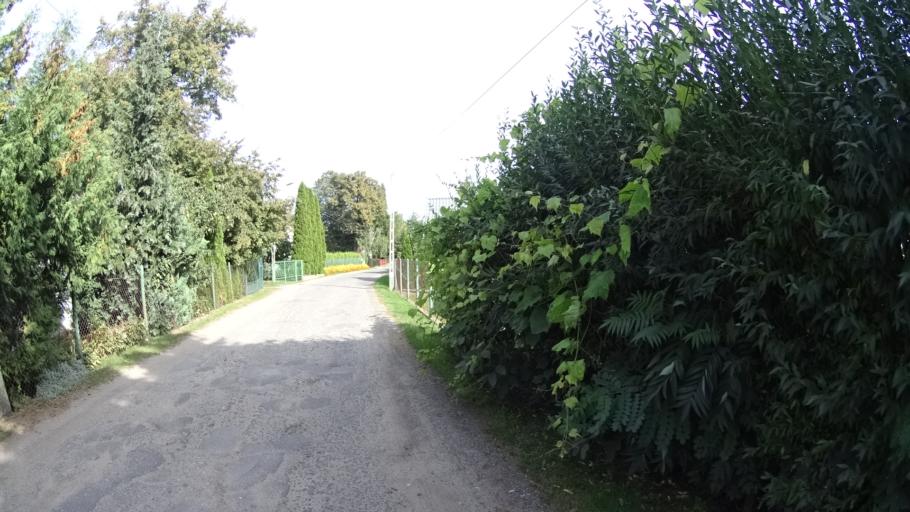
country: PL
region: Masovian Voivodeship
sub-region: Powiat legionowski
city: Serock
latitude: 52.4982
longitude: 21.0825
